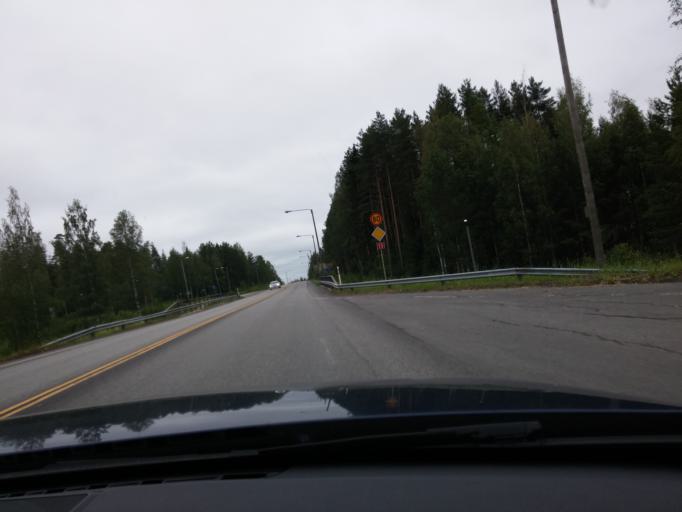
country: FI
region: Central Finland
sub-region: Saarijaervi-Viitasaari
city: Saarijaervi
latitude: 62.6893
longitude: 25.3073
